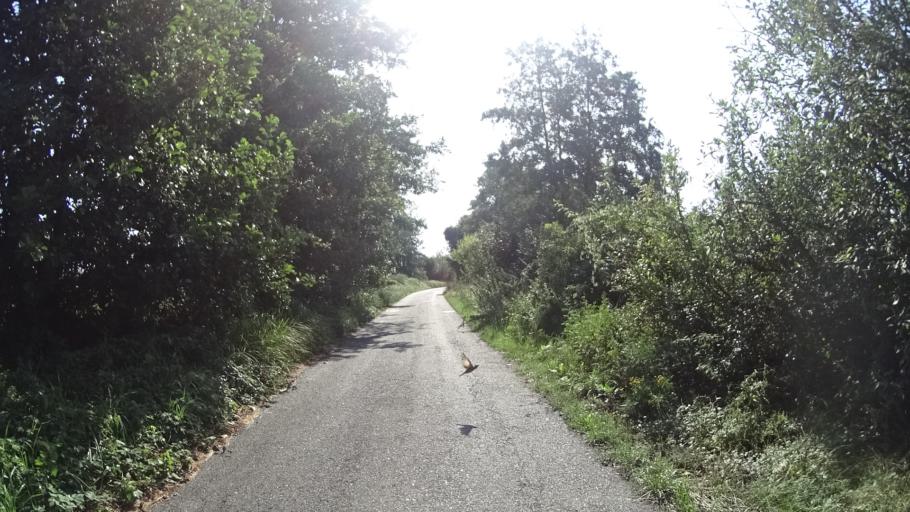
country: DE
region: Brandenburg
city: Neu Zauche
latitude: 51.9019
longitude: 14.0890
